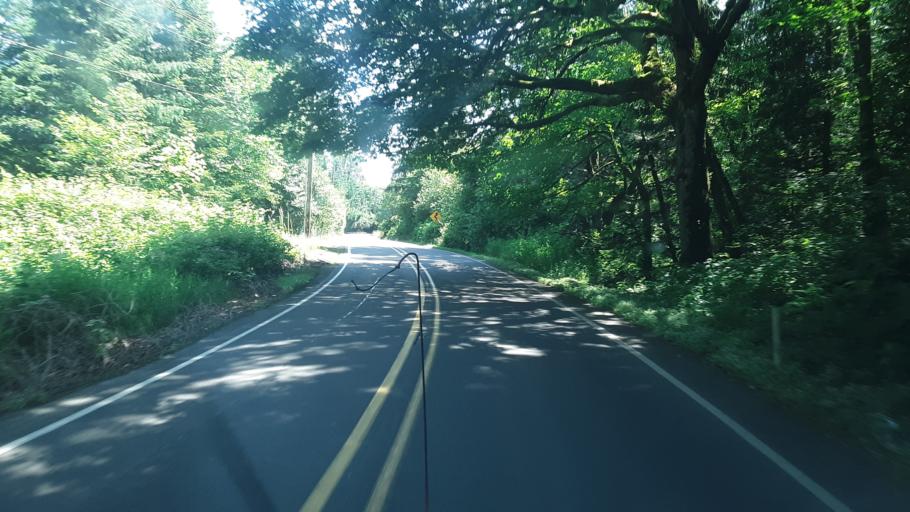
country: US
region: Washington
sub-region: Clark County
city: Amboy
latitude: 45.9000
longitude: -122.4522
